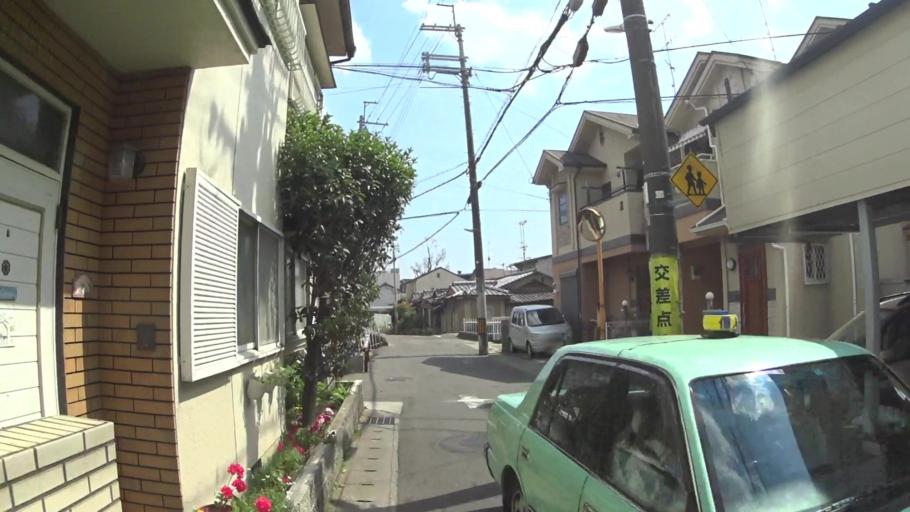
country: JP
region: Kyoto
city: Muko
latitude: 35.0132
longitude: 135.6937
